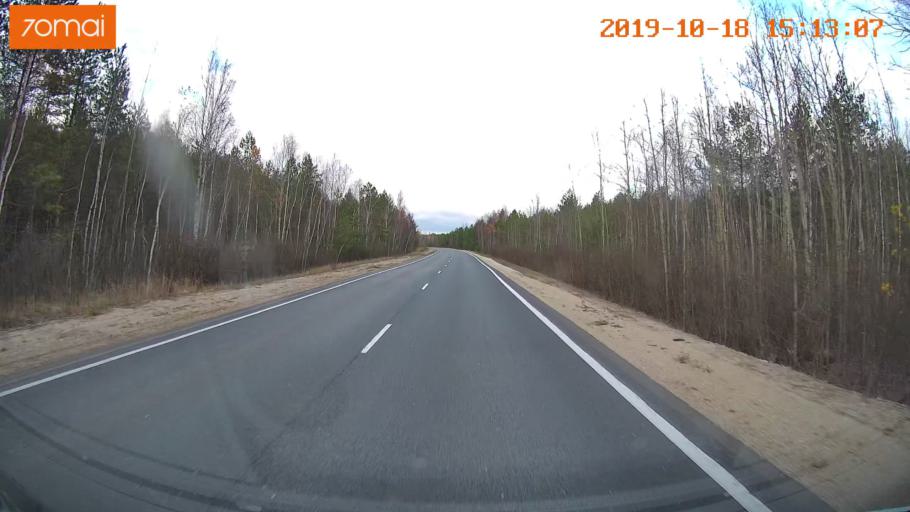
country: RU
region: Vladimir
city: Gus'-Khrustal'nyy
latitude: 55.5825
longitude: 40.7124
